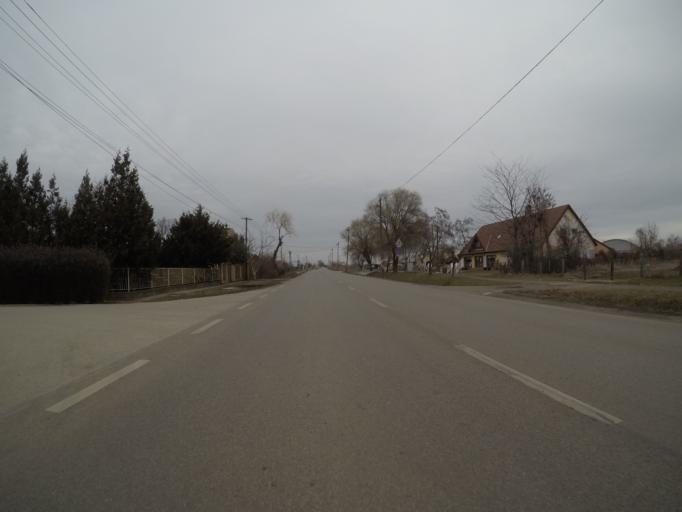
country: HU
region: Jasz-Nagykun-Szolnok
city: Jaszapati
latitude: 47.5209
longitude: 20.1525
